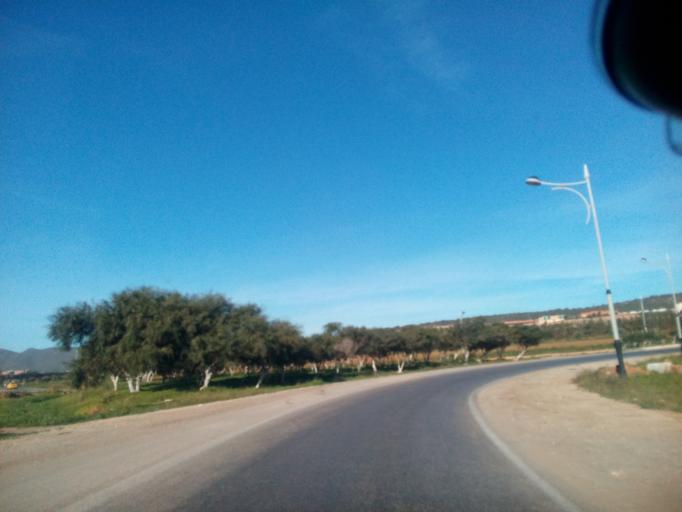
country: DZ
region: Oran
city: Bir el Djir
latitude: 35.7743
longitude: -0.4369
